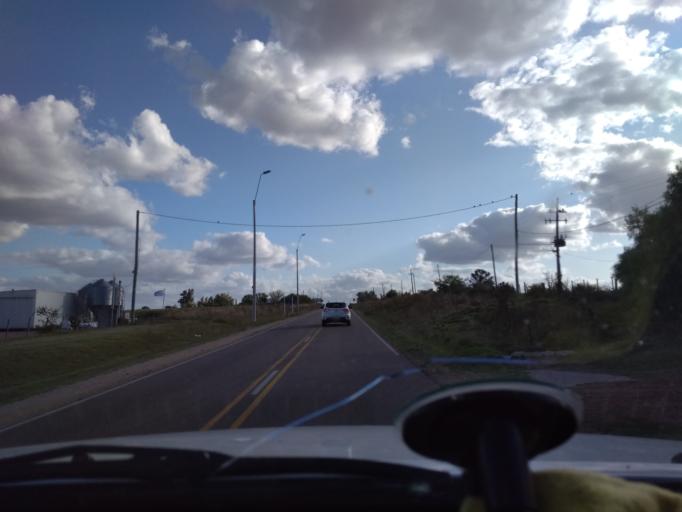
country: UY
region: Canelones
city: Tala
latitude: -34.3662
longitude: -55.7804
